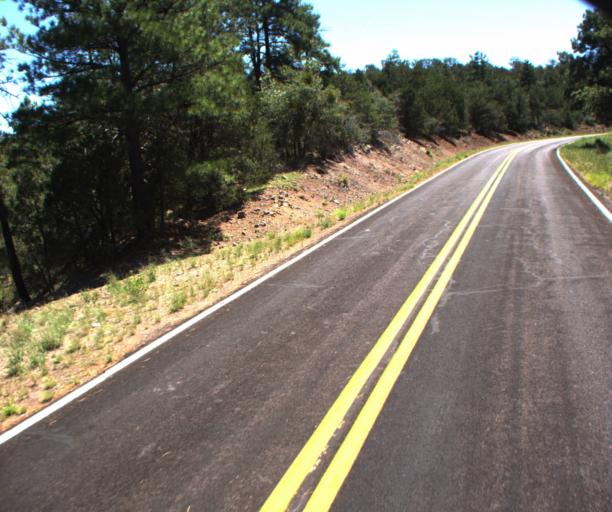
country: US
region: Arizona
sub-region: Greenlee County
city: Morenci
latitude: 33.4026
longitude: -109.3381
